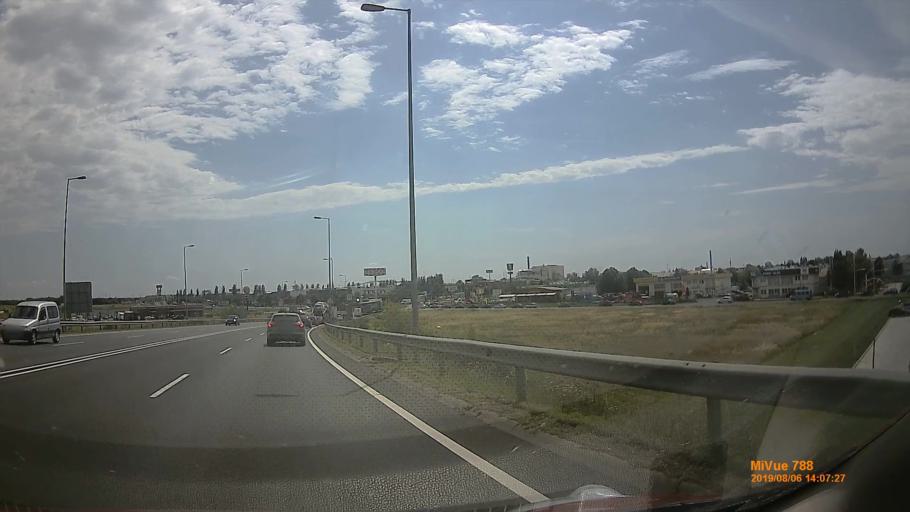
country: HU
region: Vas
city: Szombathely
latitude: 47.2444
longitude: 16.6544
